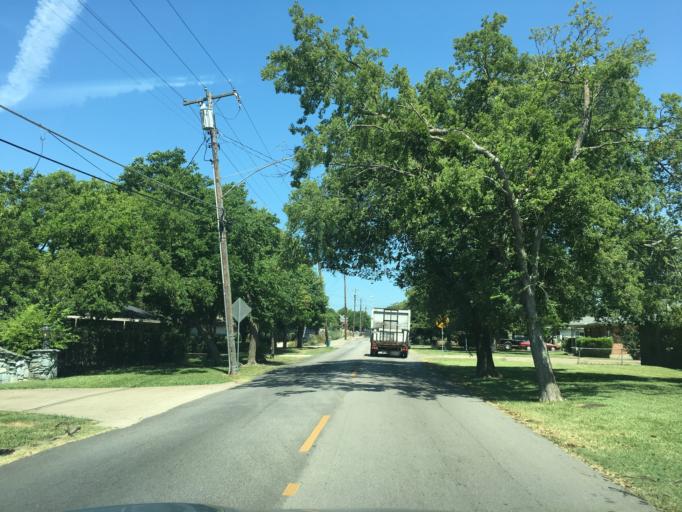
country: US
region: Texas
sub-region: Dallas County
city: Highland Park
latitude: 32.8457
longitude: -96.7407
